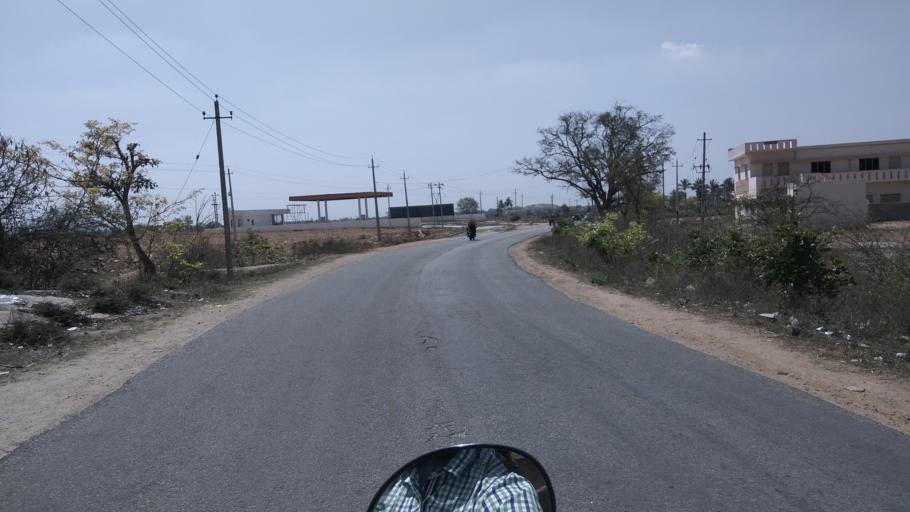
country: IN
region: Karnataka
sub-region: Kolar
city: Mulbagal
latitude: 13.1652
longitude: 78.3715
